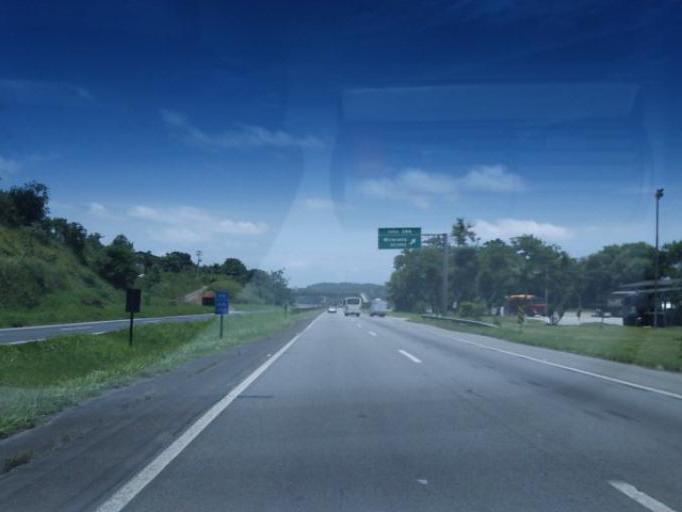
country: BR
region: Sao Paulo
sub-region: Miracatu
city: Miracatu
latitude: -24.2870
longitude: -47.4512
